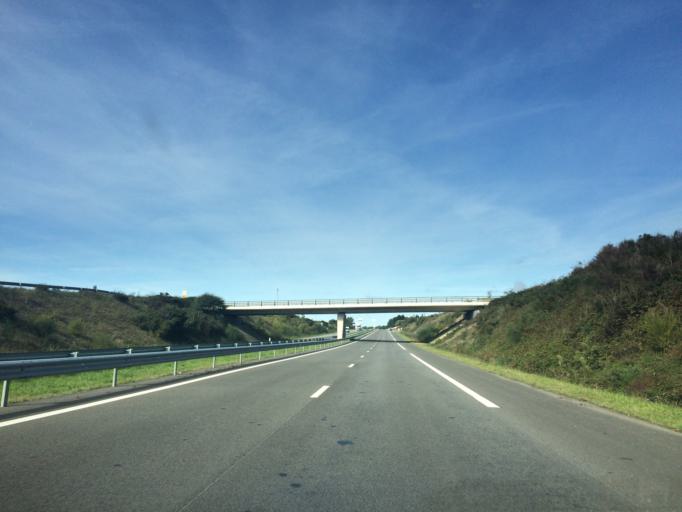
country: FR
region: Pays de la Loire
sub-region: Departement de la Loire-Atlantique
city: Sainte-Pazanne
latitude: 47.1308
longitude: -1.8338
